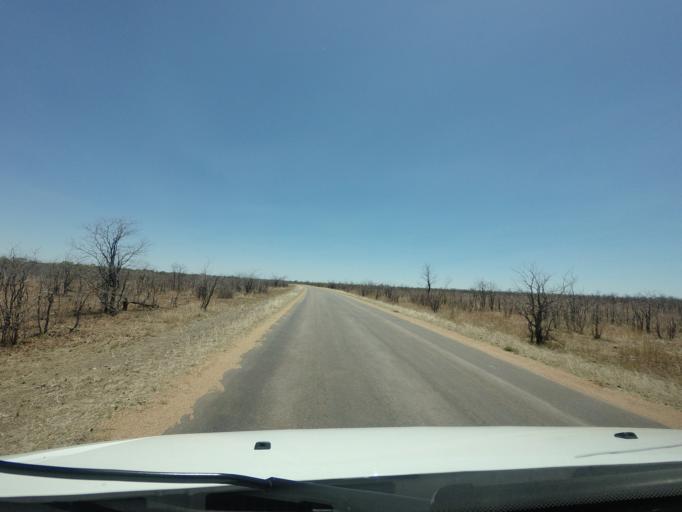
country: ZA
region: Limpopo
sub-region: Mopani District Municipality
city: Phalaborwa
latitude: -23.5607
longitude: 31.4511
